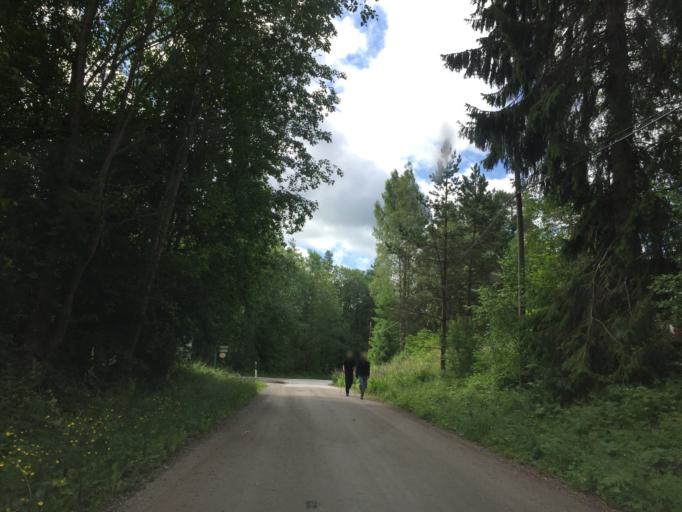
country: SE
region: OErebro
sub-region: Lekebergs Kommun
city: Fjugesta
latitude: 59.2701
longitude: 14.7965
